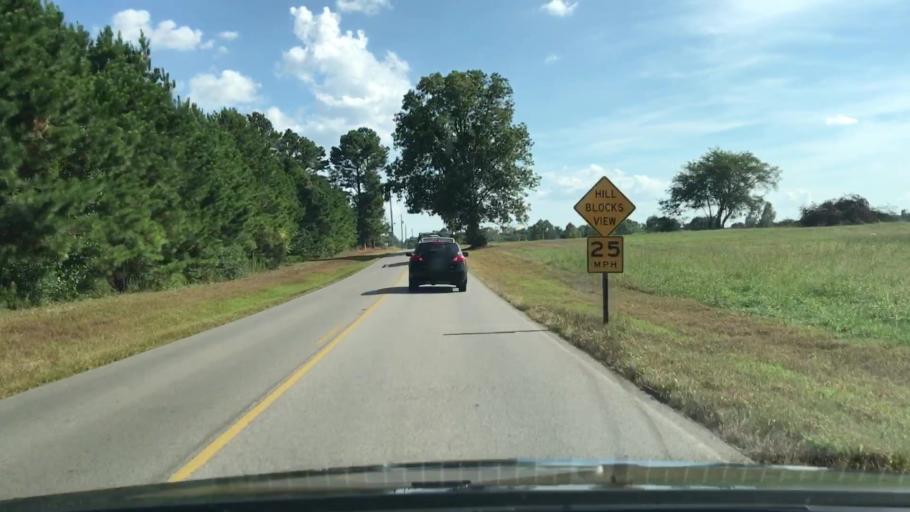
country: US
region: Alabama
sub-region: Madison County
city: Harvest
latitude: 34.8634
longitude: -86.7490
